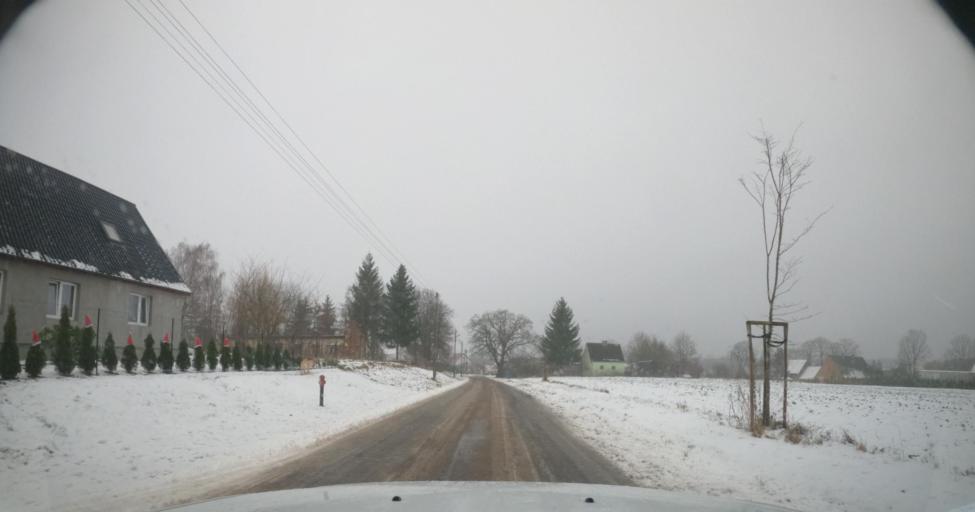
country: PL
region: West Pomeranian Voivodeship
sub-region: Powiat kamienski
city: Golczewo
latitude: 53.8092
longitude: 14.9654
